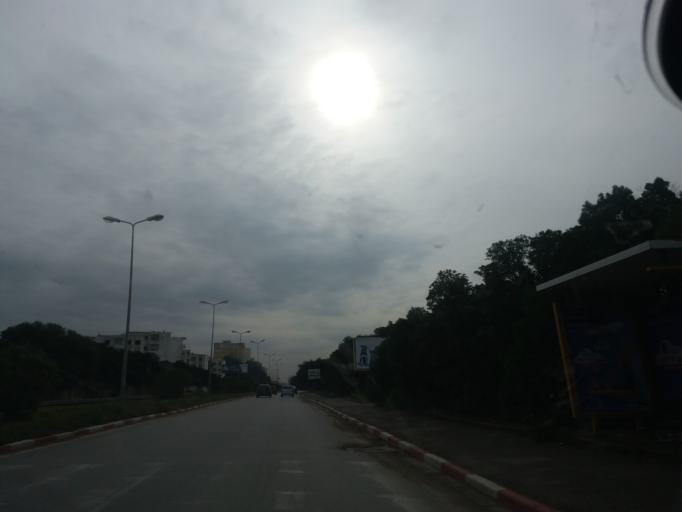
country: TN
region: Tunis
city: Tunis
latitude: 36.8490
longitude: 10.1570
